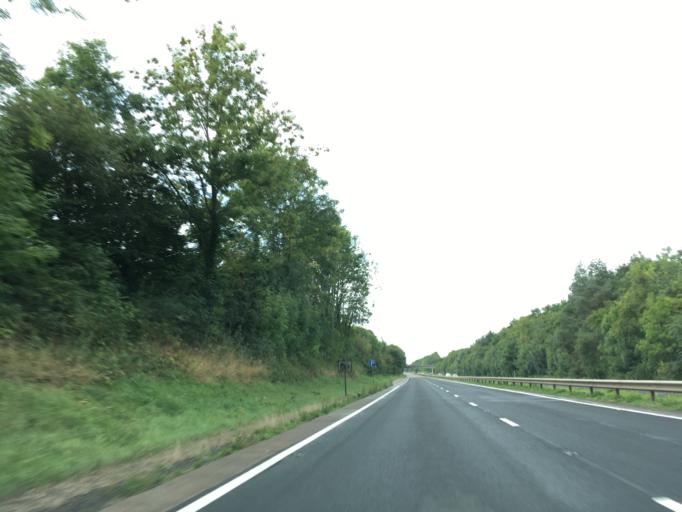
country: GB
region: Wales
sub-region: Monmouthshire
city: Llanarth
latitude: 51.7817
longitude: -2.9185
